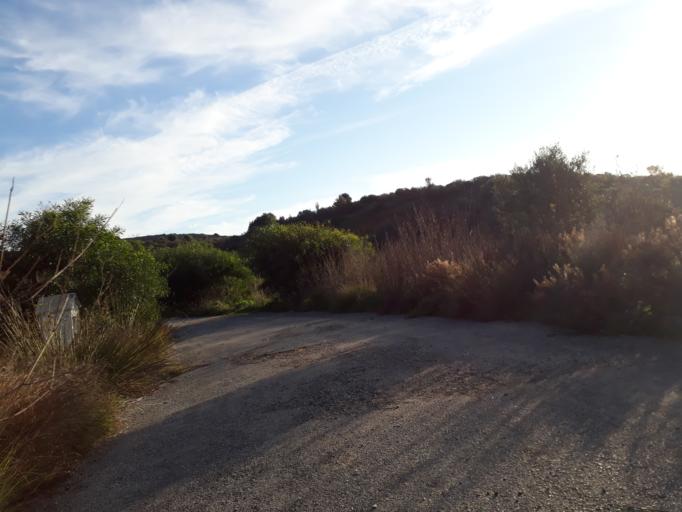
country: ES
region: Andalusia
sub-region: Provincia de Malaga
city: Fuengirola
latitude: 36.5032
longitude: -4.6991
